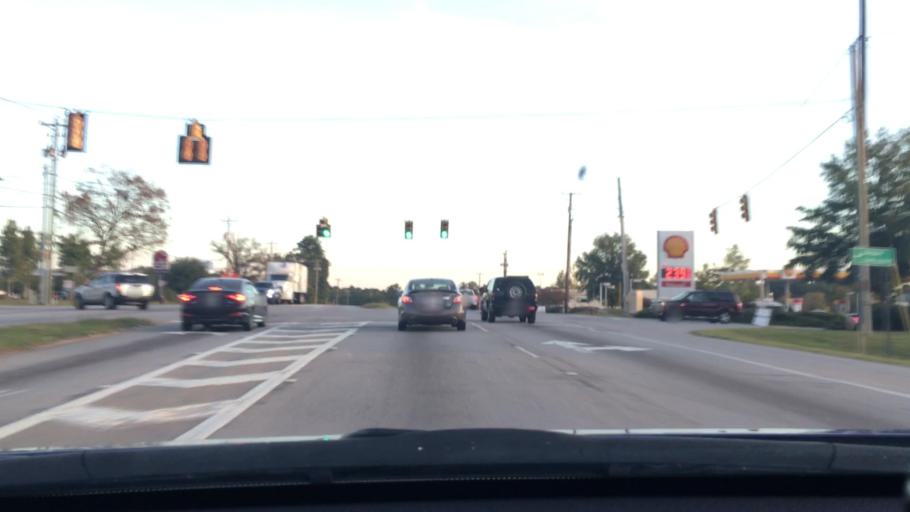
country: US
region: South Carolina
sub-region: Richland County
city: Forest Acres
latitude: 33.9632
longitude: -80.9421
